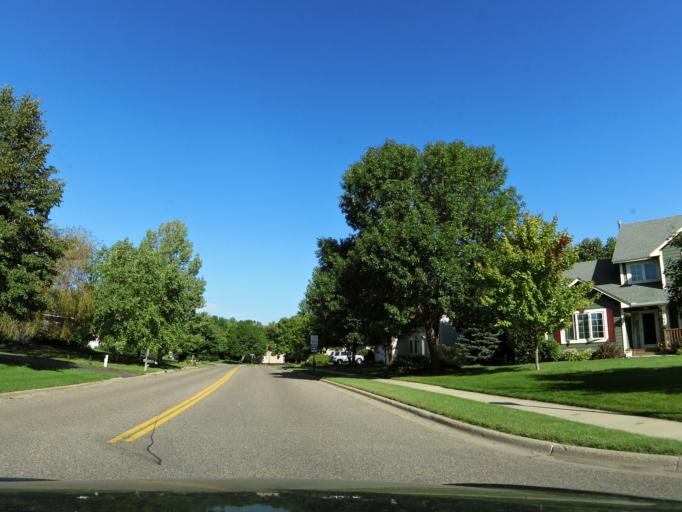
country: US
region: Minnesota
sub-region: Scott County
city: Savage
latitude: 44.7366
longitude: -93.3368
